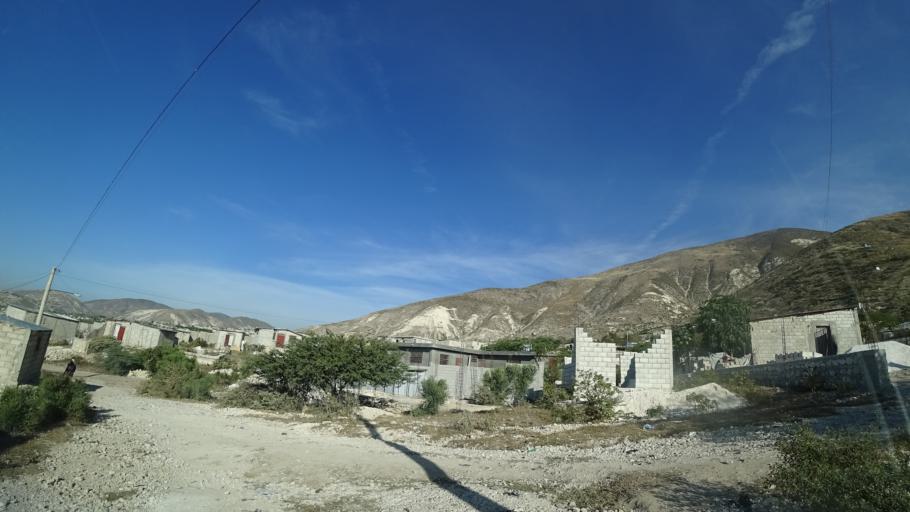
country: HT
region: Ouest
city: Croix des Bouquets
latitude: 18.6708
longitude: -72.2261
